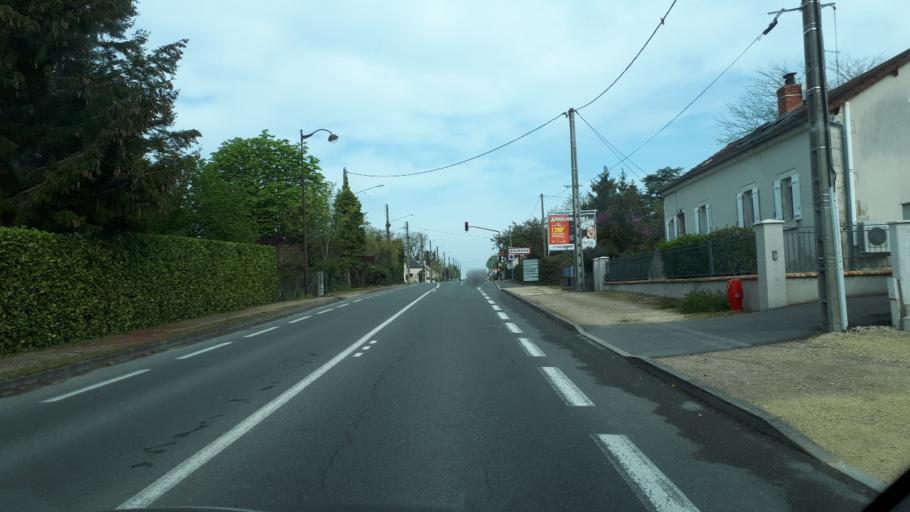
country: FR
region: Centre
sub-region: Departement du Cher
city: Bourges
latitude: 47.0595
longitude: 2.4251
